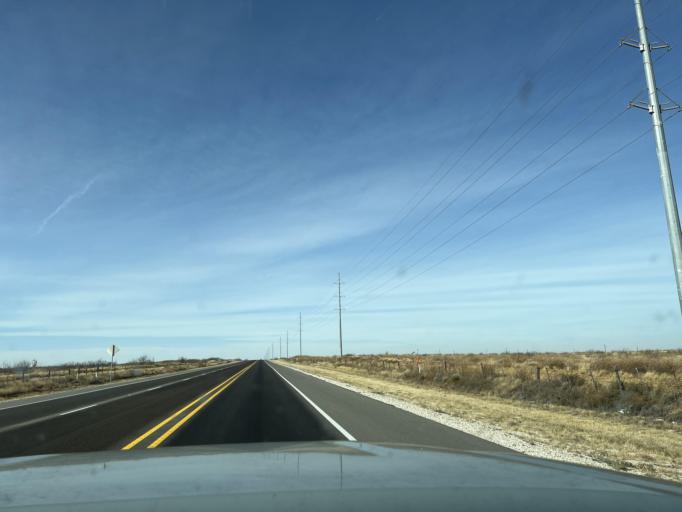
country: US
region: Texas
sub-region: Andrews County
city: Andrews
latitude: 32.3515
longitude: -102.7398
